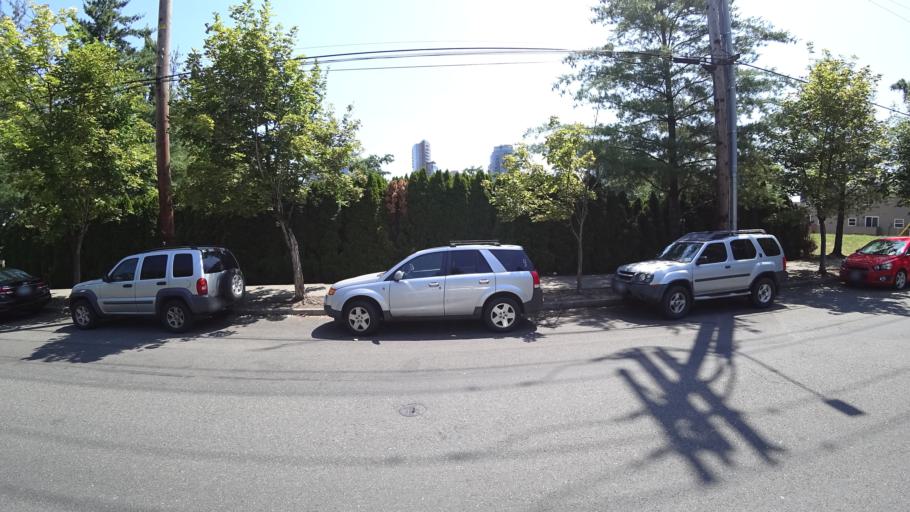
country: US
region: Oregon
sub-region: Multnomah County
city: Portland
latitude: 45.4977
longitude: -122.6750
